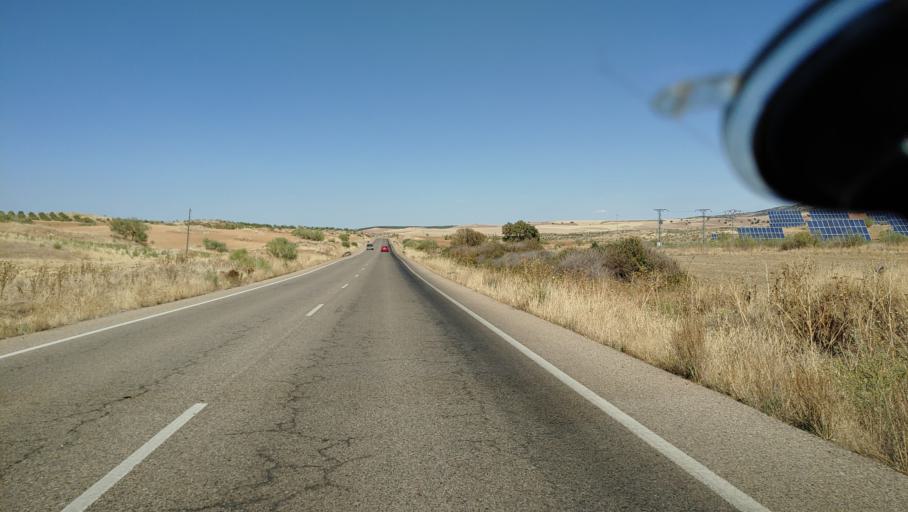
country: ES
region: Castille-La Mancha
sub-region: Province of Toledo
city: Casasbuenas
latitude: 39.7340
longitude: -4.1062
